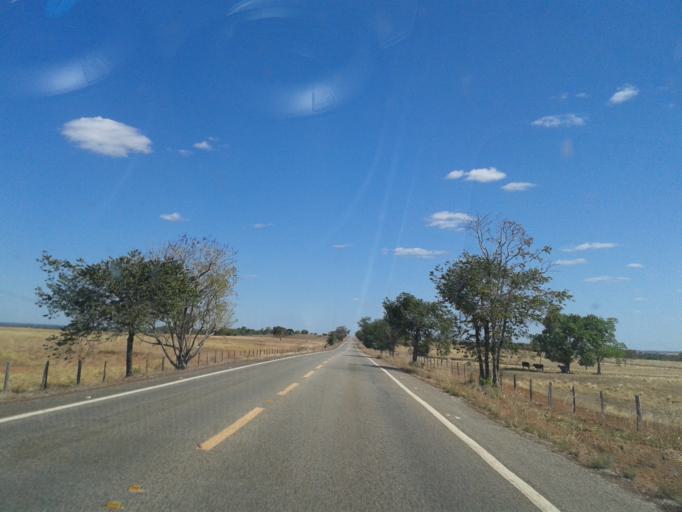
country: BR
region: Goias
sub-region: Sao Miguel Do Araguaia
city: Sao Miguel do Araguaia
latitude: -13.4061
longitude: -50.2624
